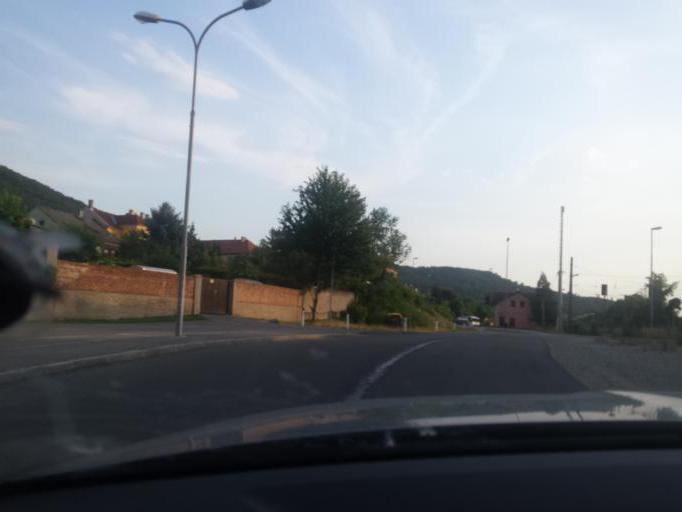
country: AT
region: Lower Austria
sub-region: Politischer Bezirk Bruck an der Leitha
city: Hainburg an der Donau
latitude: 48.1460
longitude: 16.9342
